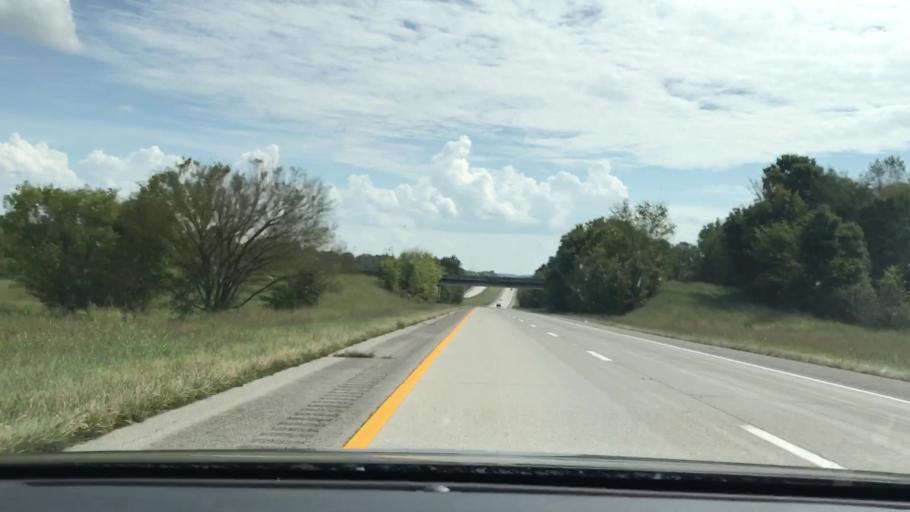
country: US
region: Kentucky
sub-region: Trigg County
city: Cadiz
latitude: 36.9369
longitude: -87.8247
